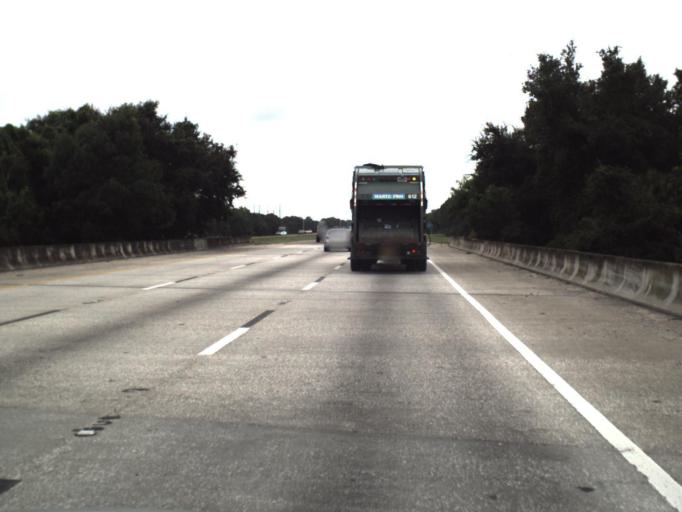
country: US
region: Florida
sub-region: Sarasota County
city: The Meadows
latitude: 27.4127
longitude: -82.4557
